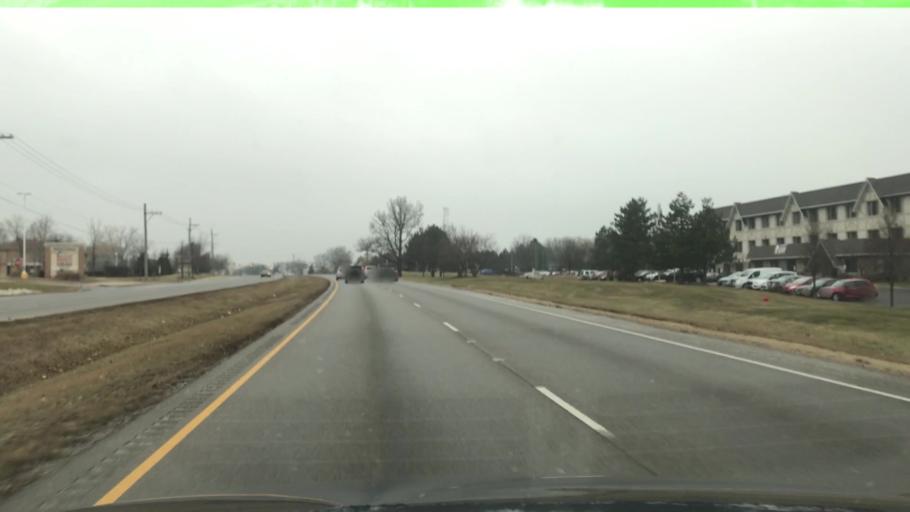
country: US
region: Illinois
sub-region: Lake County
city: Lake Zurich
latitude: 42.1816
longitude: -88.0816
